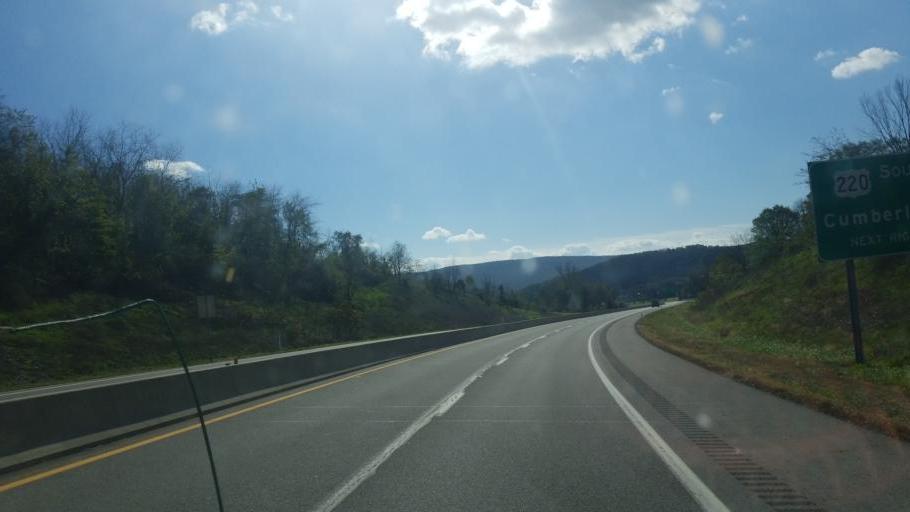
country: US
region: Pennsylvania
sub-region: Bedford County
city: Bedford
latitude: 40.0332
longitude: -78.5177
